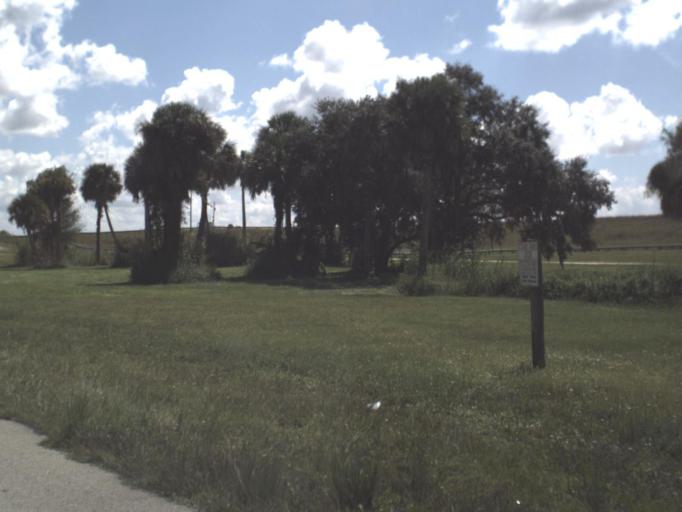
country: US
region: Florida
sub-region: Okeechobee County
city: Taylor Creek
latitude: 27.1954
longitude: -80.7649
